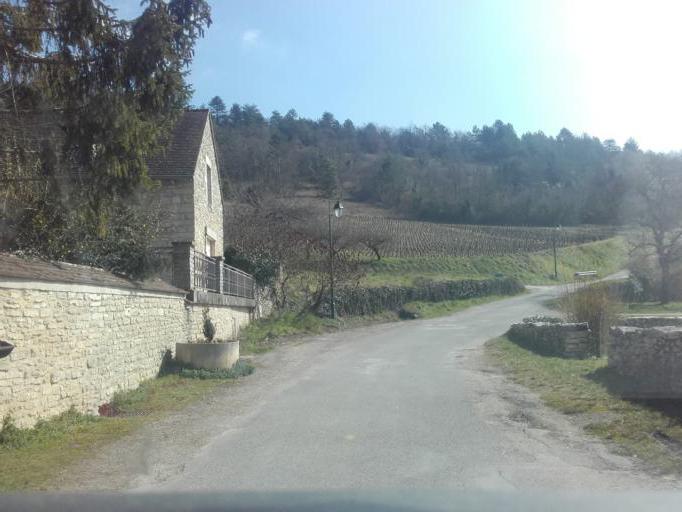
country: FR
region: Bourgogne
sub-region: Departement de la Cote-d'Or
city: Meursault
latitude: 47.0323
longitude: 4.7619
